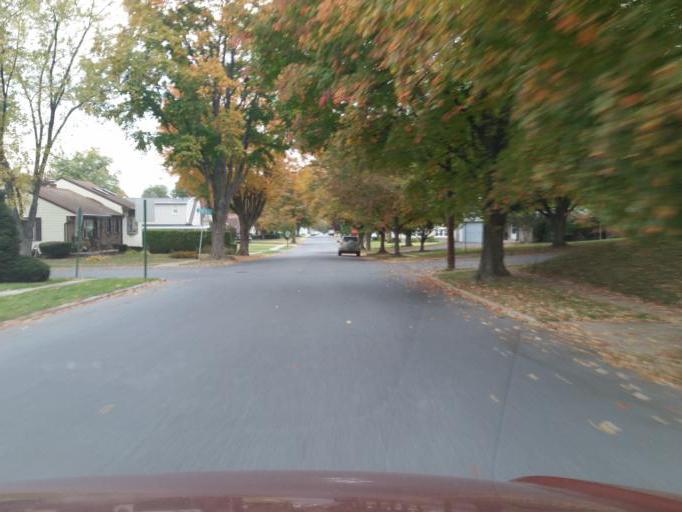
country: US
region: Pennsylvania
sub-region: Dauphin County
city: Hummelstown
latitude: 40.2605
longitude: -76.7144
